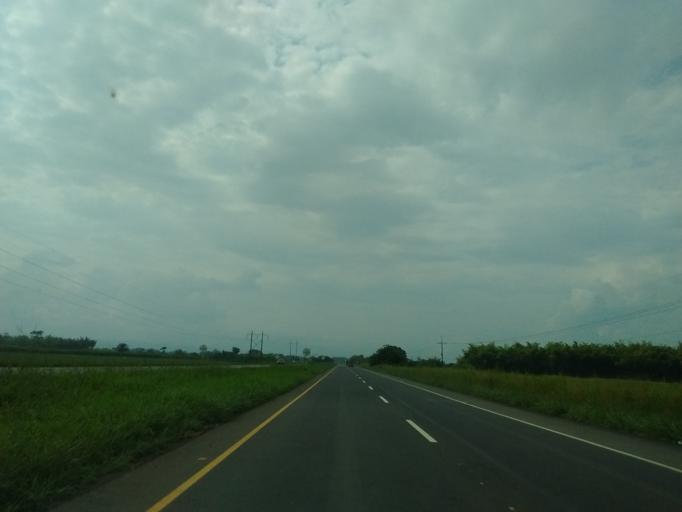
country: CO
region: Cauca
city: Caloto
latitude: 3.1007
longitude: -76.4691
